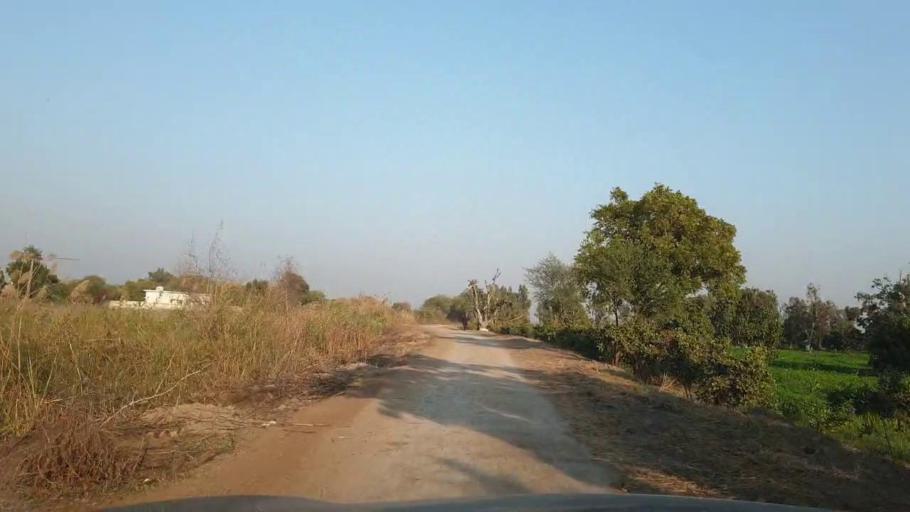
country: PK
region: Sindh
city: Tando Allahyar
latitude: 25.5464
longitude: 68.8539
